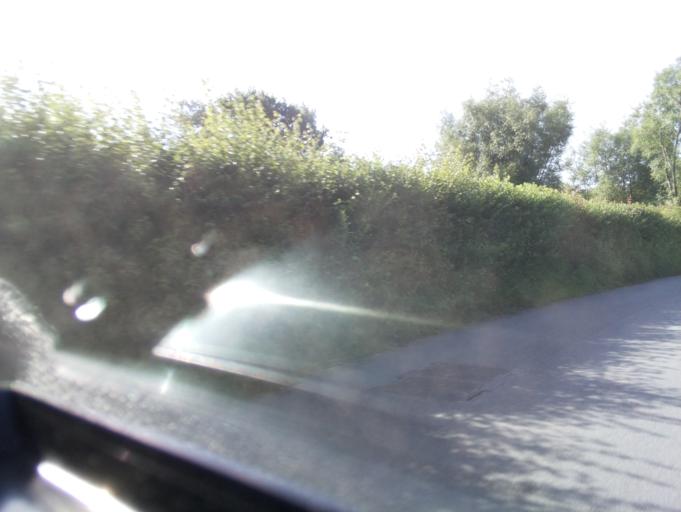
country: GB
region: England
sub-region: South Gloucestershire
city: Bitton
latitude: 51.4293
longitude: -2.4539
